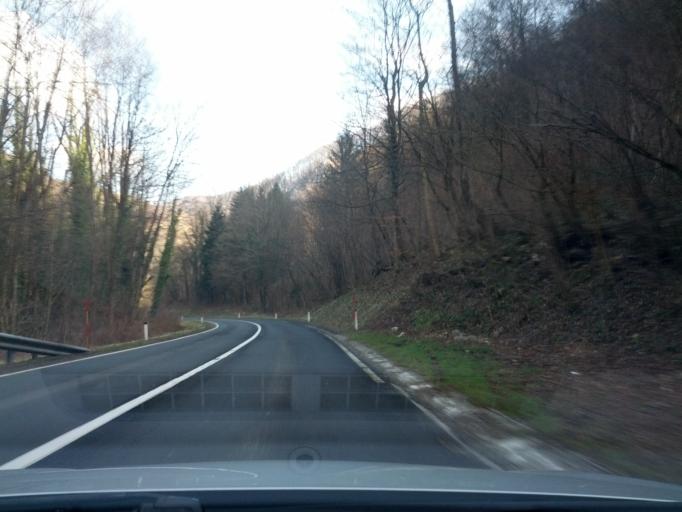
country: SI
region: Zagorje ob Savi
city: Kisovec
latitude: 46.0970
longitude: 14.9577
